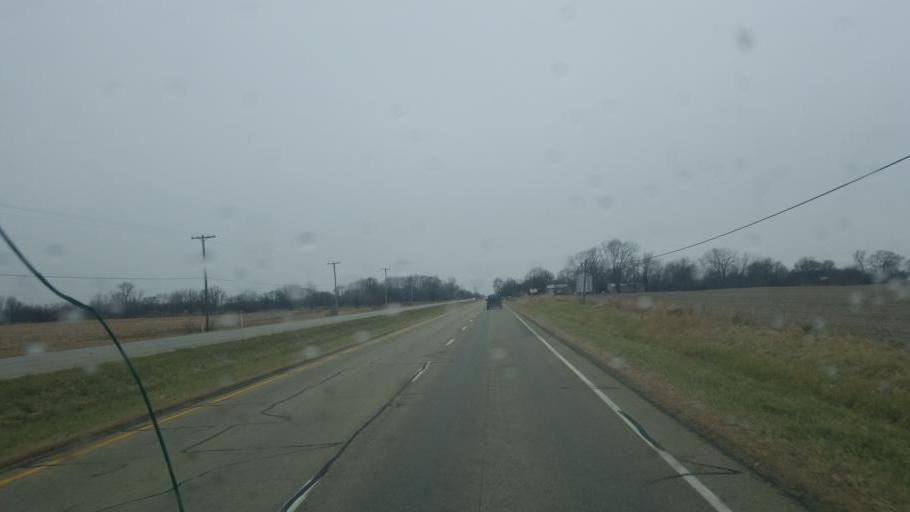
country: US
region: Indiana
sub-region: Henry County
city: Knightstown
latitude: 39.7908
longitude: -85.6372
